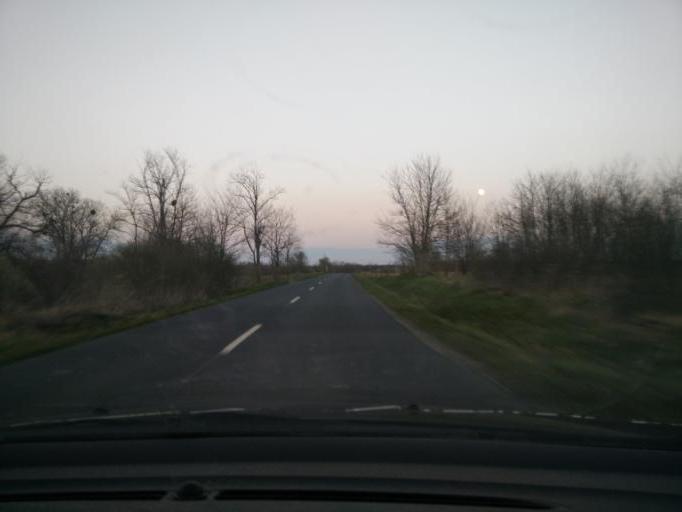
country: HU
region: Veszprem
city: Devecser
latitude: 47.0728
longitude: 17.3784
